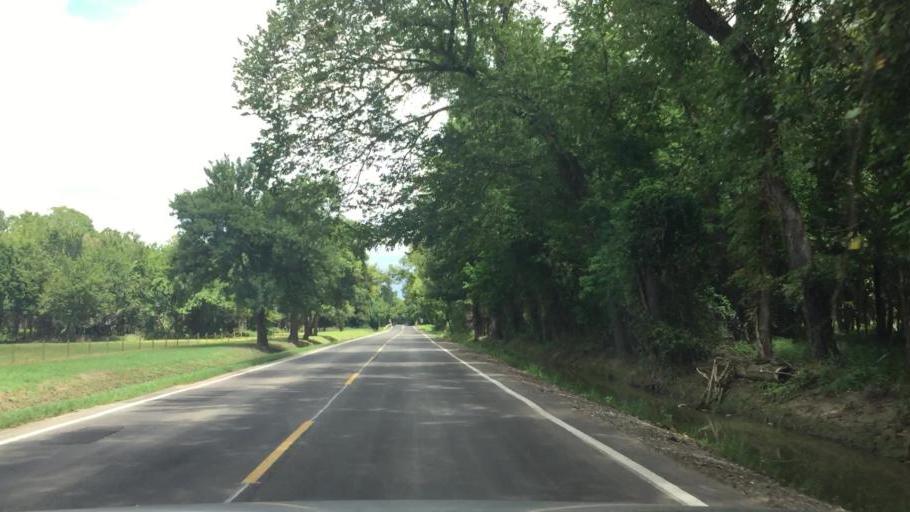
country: US
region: Texas
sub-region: Harris County
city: Jersey Village
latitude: 29.8133
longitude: -95.6363
